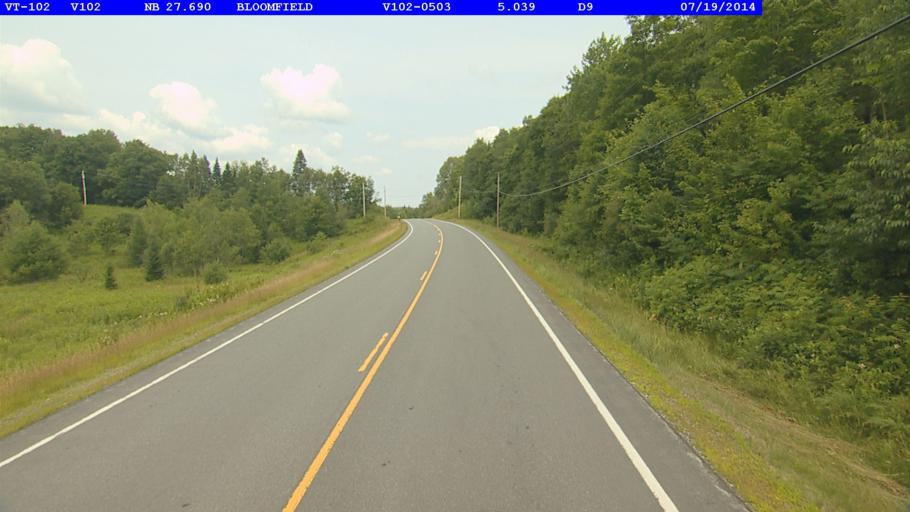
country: US
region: New Hampshire
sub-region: Coos County
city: Colebrook
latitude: 44.8032
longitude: -71.5730
